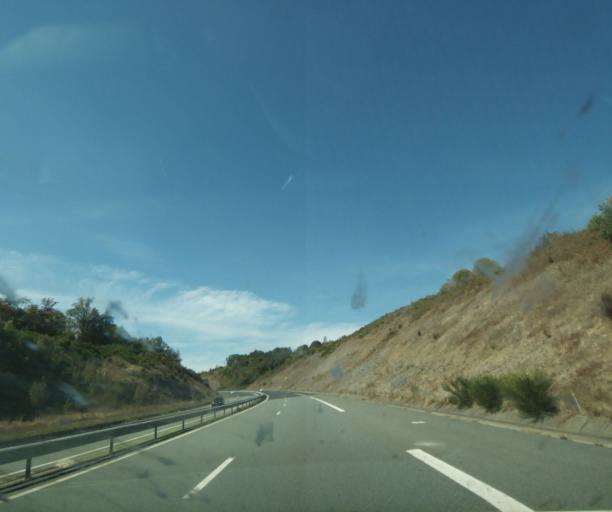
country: FR
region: Limousin
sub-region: Departement de la Correze
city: Naves
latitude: 45.3212
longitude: 1.7845
